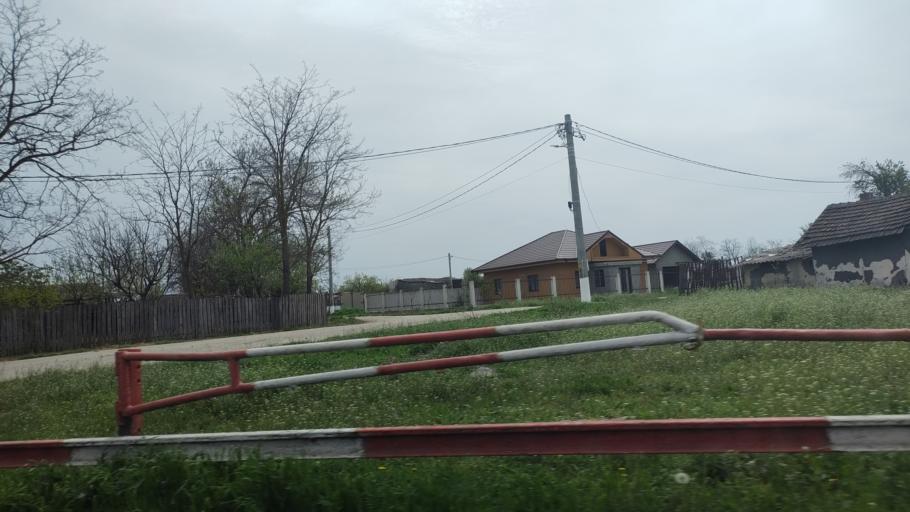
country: RO
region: Constanta
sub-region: Comuna Ciocarlia
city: Ciocarlia
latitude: 44.1028
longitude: 28.2785
